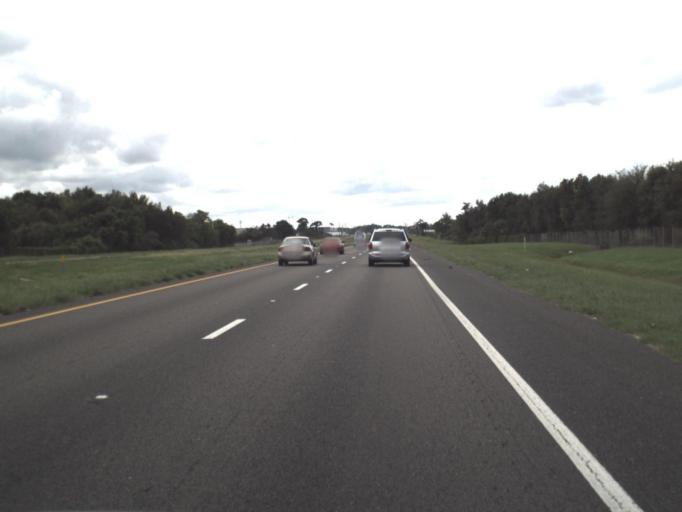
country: US
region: Florida
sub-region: Manatee County
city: Whitfield
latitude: 27.4120
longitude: -82.5331
